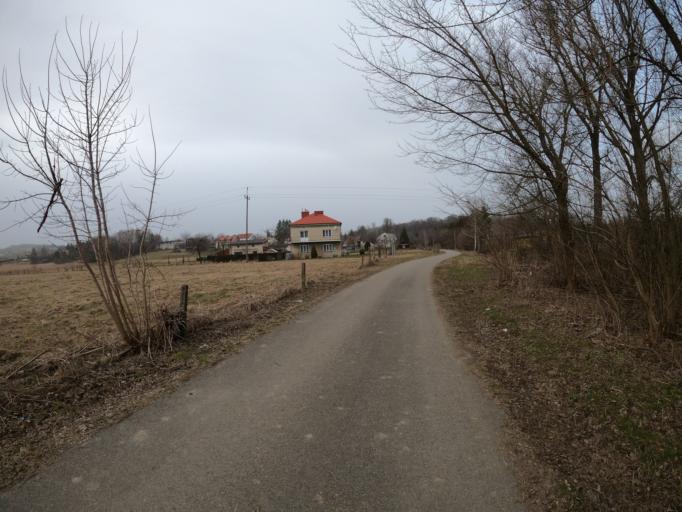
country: PL
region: Subcarpathian Voivodeship
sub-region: Powiat strzyzowski
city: Wisniowa
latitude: 49.8637
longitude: 21.6427
